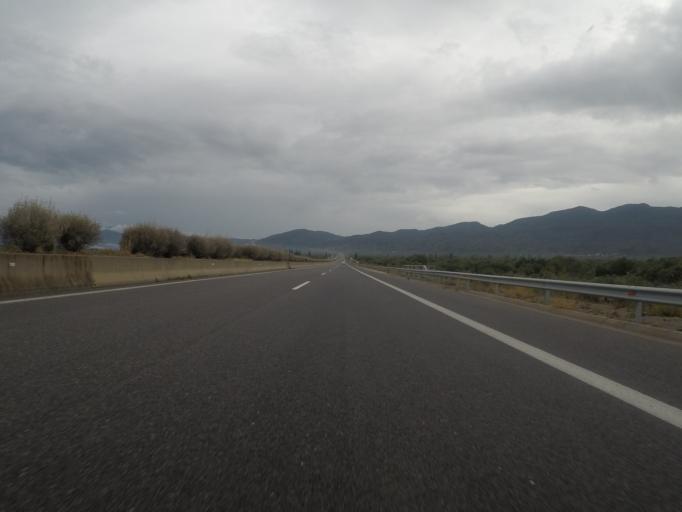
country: GR
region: Peloponnese
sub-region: Nomos Messinias
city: Meligalas
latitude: 37.2163
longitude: 22.0041
